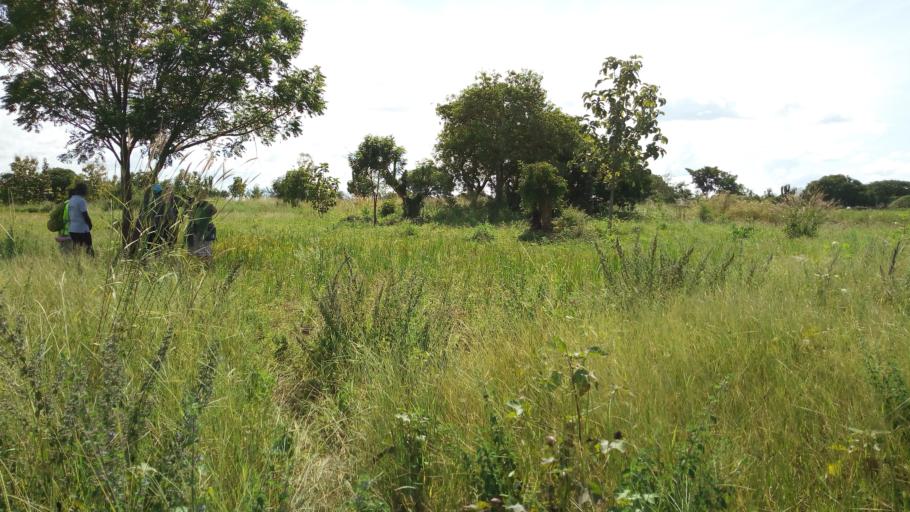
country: UG
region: Northern Region
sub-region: Adjumani District
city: Adjumani
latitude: 3.4554
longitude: 31.8943
